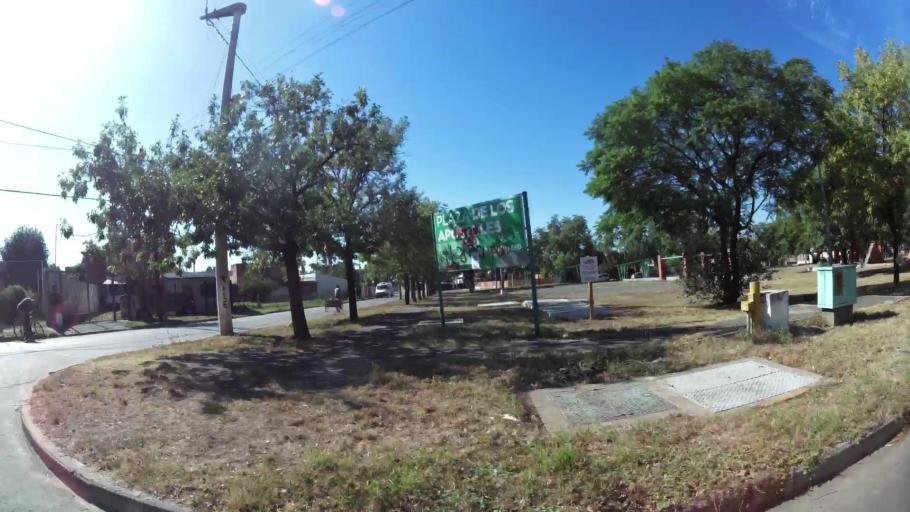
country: AR
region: Cordoba
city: Villa Allende
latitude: -31.3453
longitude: -64.2420
